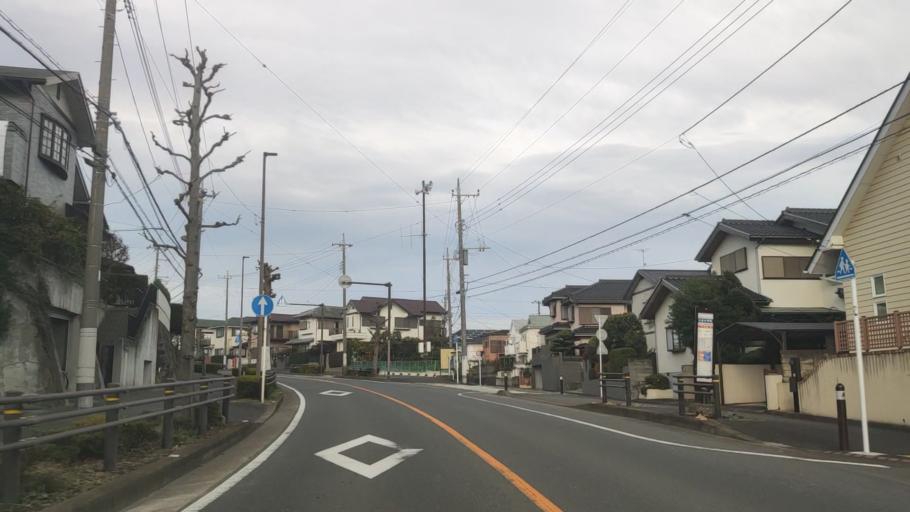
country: JP
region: Kanagawa
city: Atsugi
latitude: 35.4412
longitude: 139.4026
